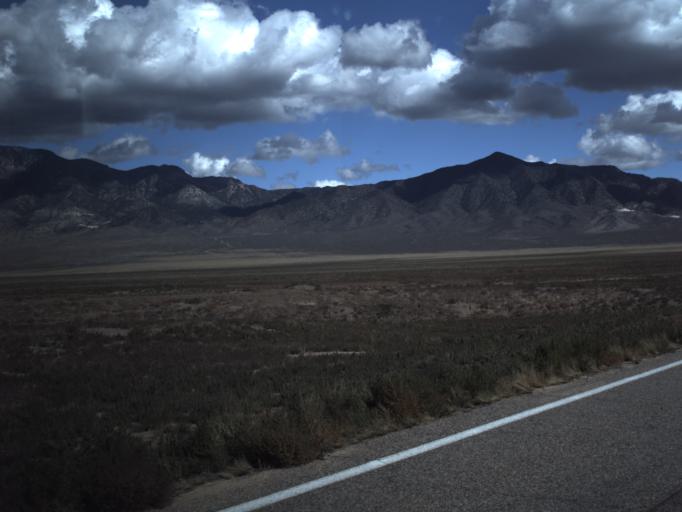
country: US
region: Utah
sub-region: Beaver County
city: Milford
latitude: 38.4637
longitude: -113.3862
